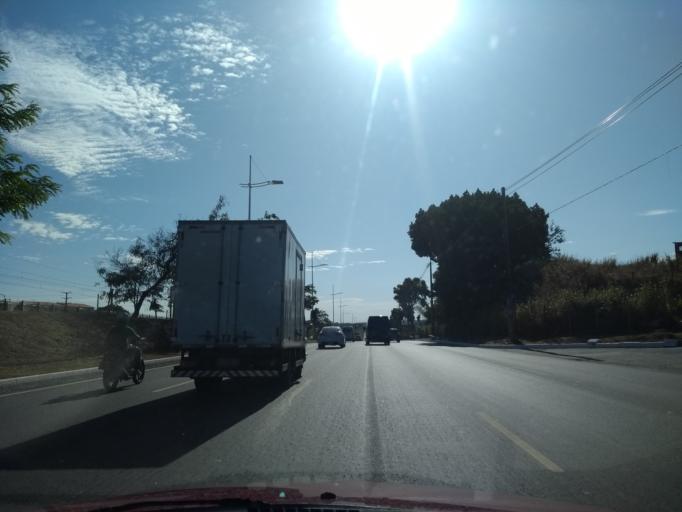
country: BR
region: Bahia
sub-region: Lauro De Freitas
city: Lauro de Freitas
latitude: -12.9229
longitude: -38.3679
